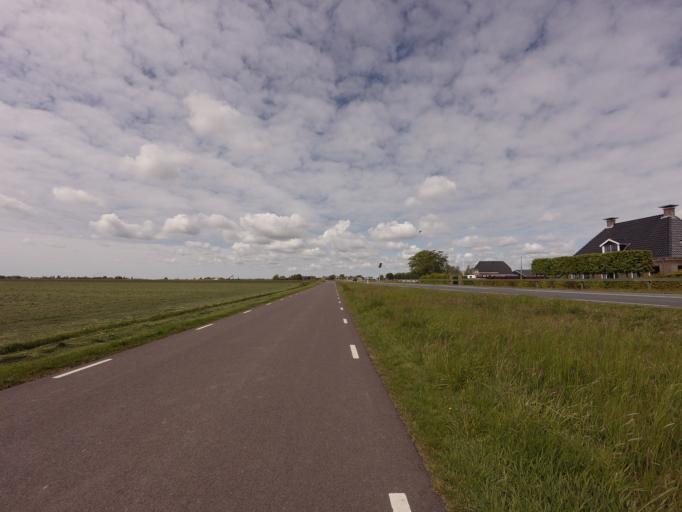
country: NL
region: Friesland
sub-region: Sudwest Fryslan
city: Woudsend
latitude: 52.9621
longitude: 5.6515
